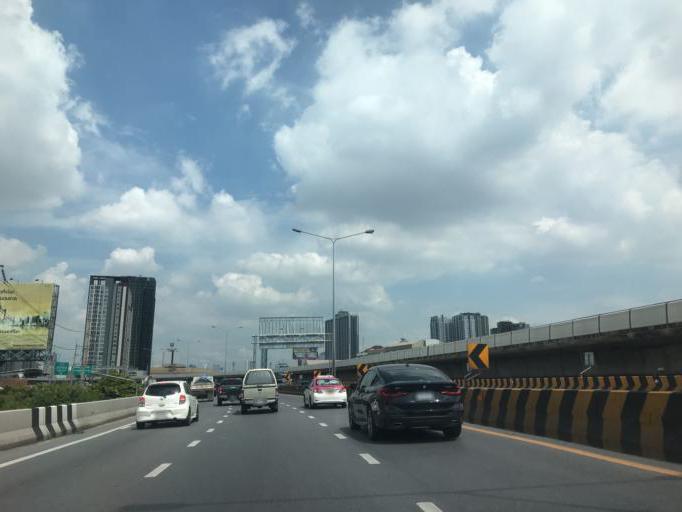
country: TH
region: Bangkok
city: Bangkok Yai
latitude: 13.7124
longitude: 100.4718
